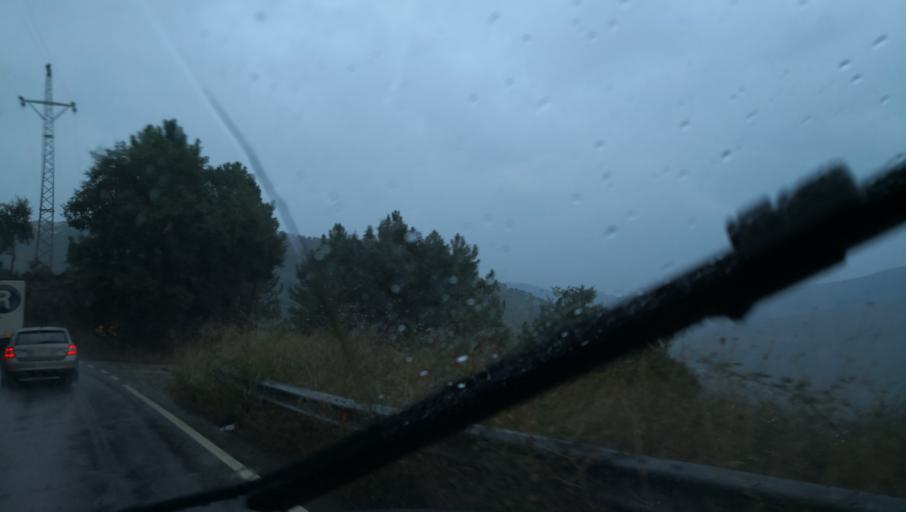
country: PT
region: Vila Real
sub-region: Santa Marta de Penaguiao
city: Santa Marta de Penaguiao
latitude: 41.2176
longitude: -7.7285
